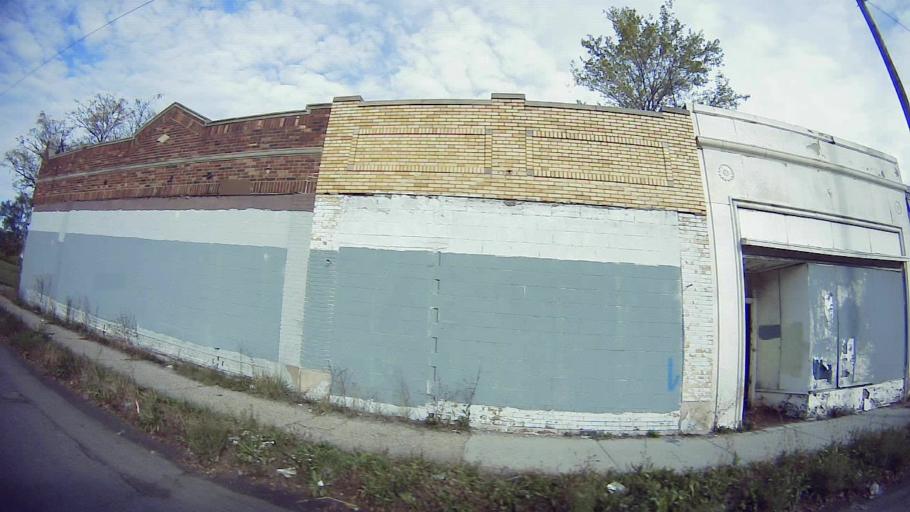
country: US
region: Michigan
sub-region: Oakland County
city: Oak Park
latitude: 42.4022
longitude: -83.1767
